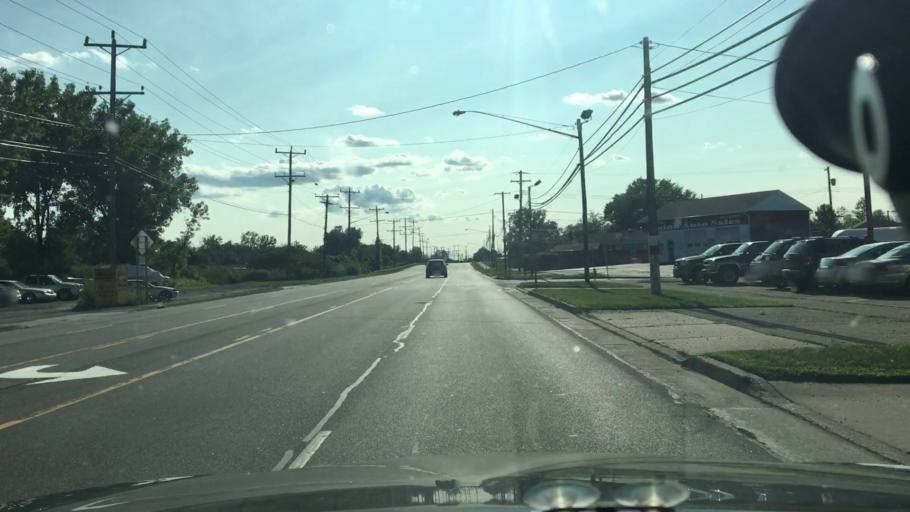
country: US
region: New York
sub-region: Erie County
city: Depew
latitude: 42.9097
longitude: -78.7113
